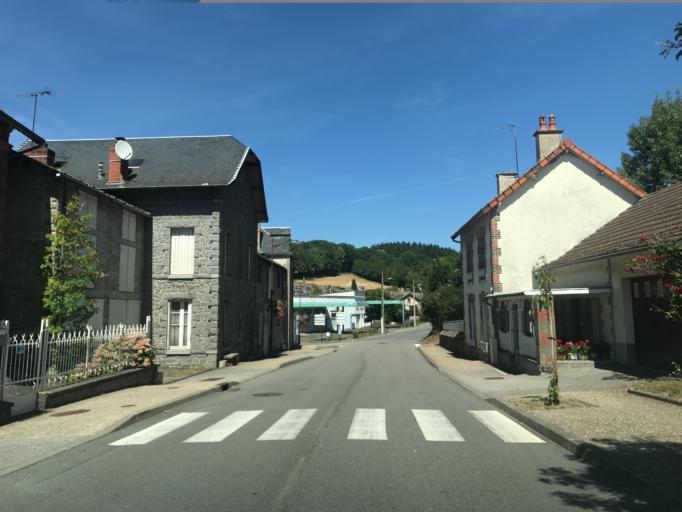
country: FR
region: Limousin
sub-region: Departement de la Creuse
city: Felletin
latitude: 45.8867
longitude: 2.1741
